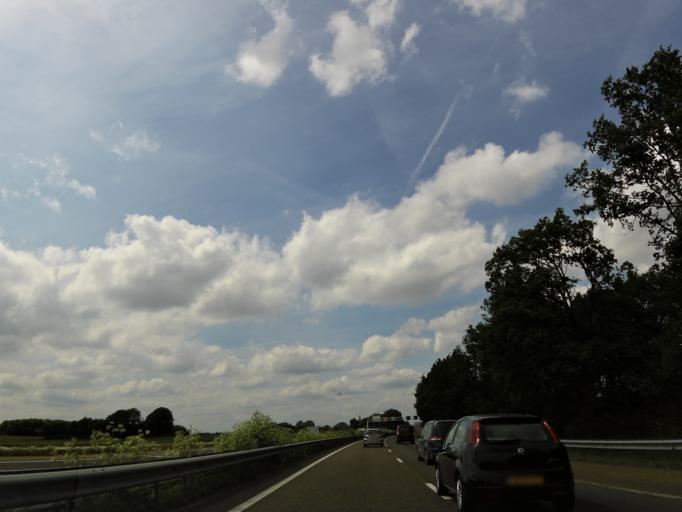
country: NL
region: Limburg
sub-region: Gemeente Beek
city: Beek
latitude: 50.9476
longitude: 5.8323
